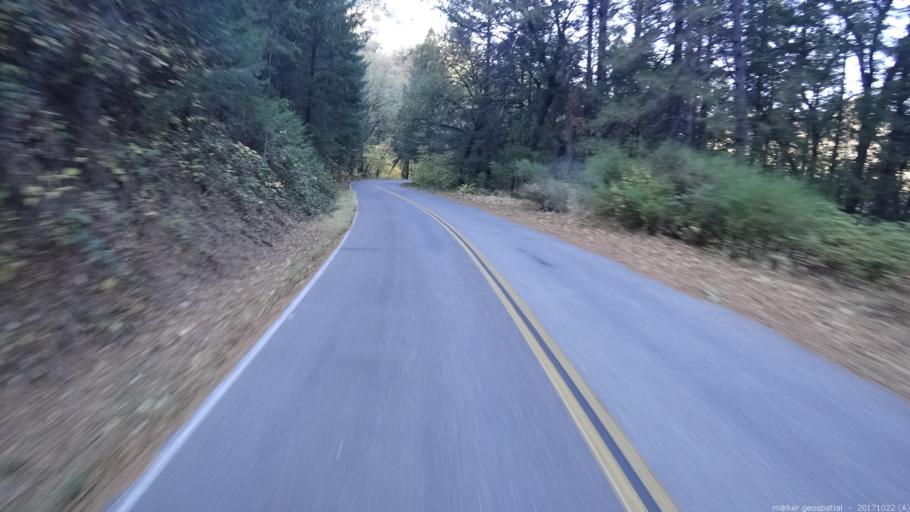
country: US
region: California
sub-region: Shasta County
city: Shasta Lake
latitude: 40.9274
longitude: -122.2496
